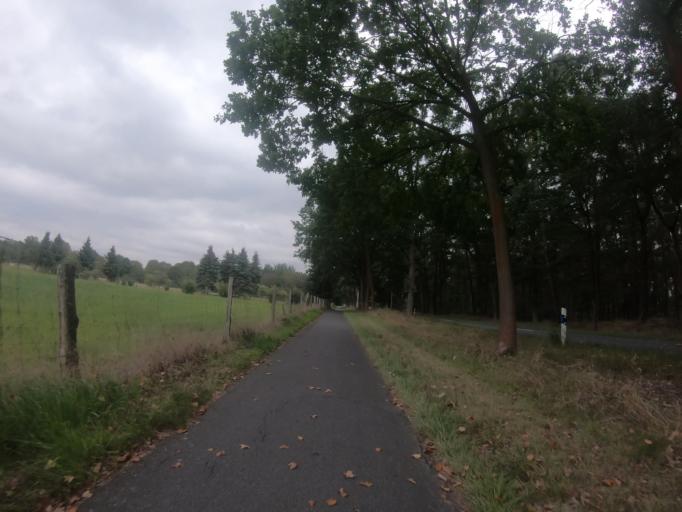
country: DE
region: Lower Saxony
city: Ribbesbuttel
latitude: 52.4464
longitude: 10.5013
